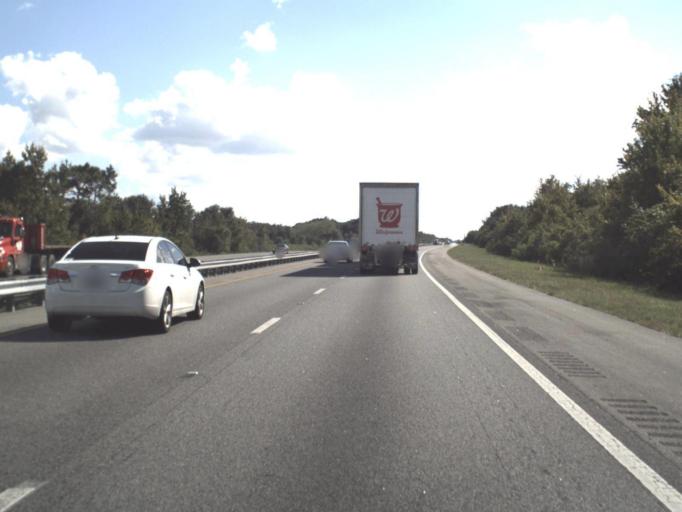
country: US
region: Florida
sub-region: Brevard County
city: June Park
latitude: 27.8563
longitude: -81.0088
